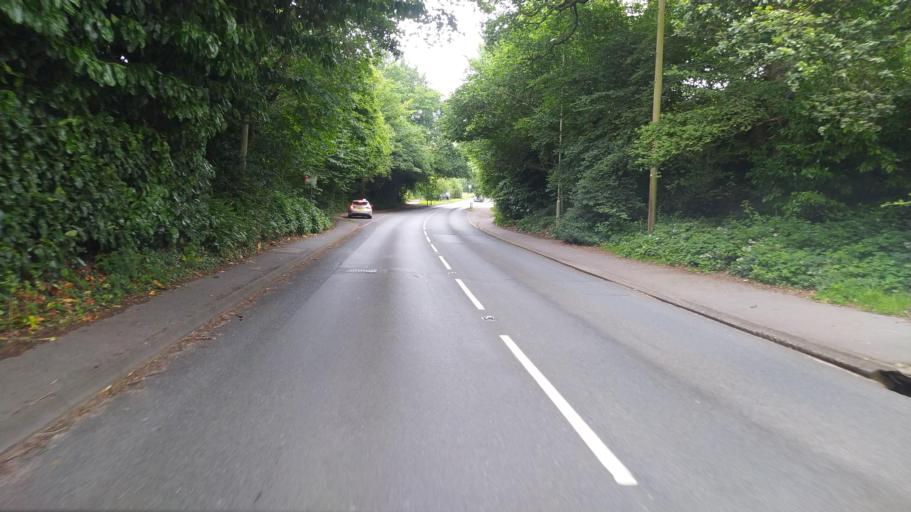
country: GB
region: England
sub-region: Hampshire
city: Liphook
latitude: 51.0817
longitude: -0.8009
